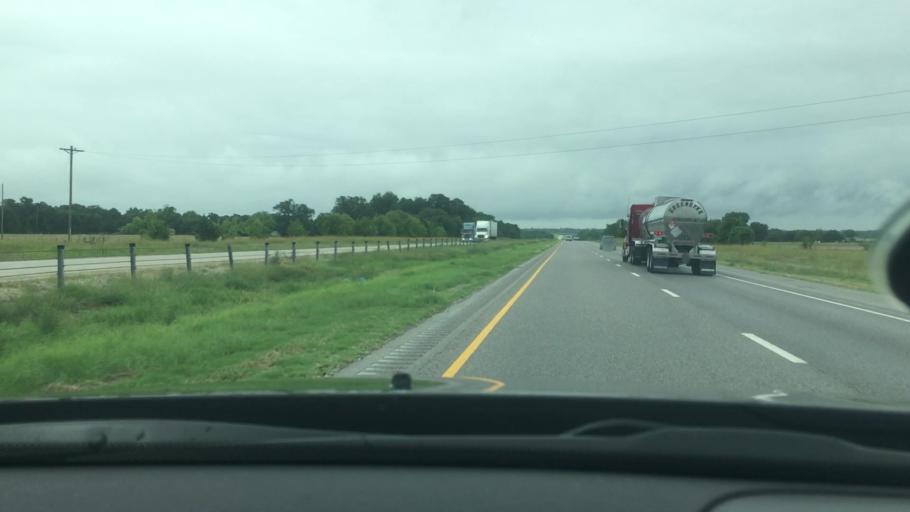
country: US
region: Oklahoma
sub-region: Bryan County
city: Durant
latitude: 34.0772
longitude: -96.3385
